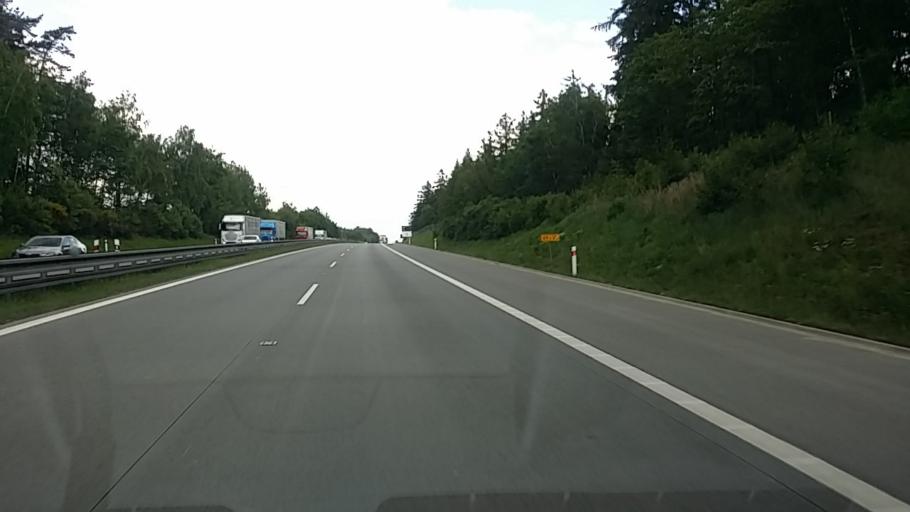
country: CZ
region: Central Bohemia
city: Cechtice
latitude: 49.6314
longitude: 15.1294
